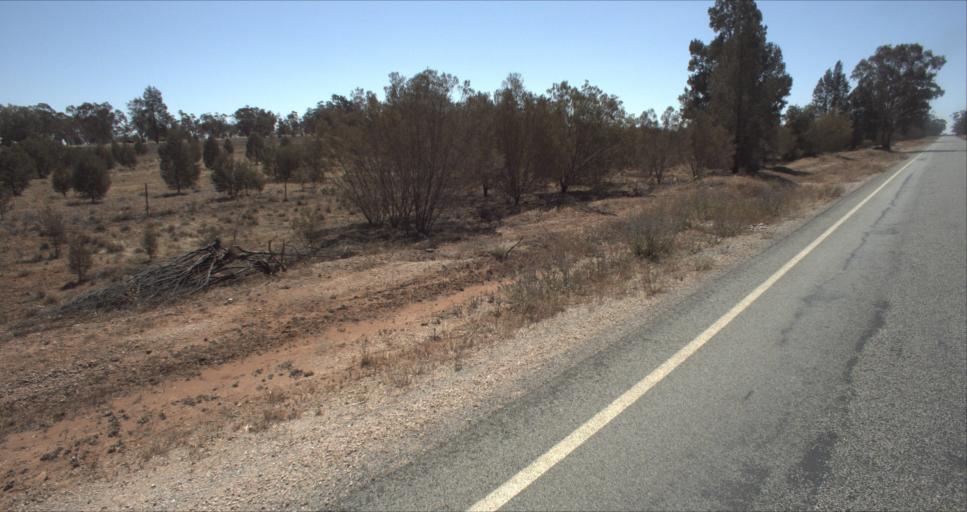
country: AU
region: New South Wales
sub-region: Leeton
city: Leeton
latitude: -34.4847
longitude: 146.4335
